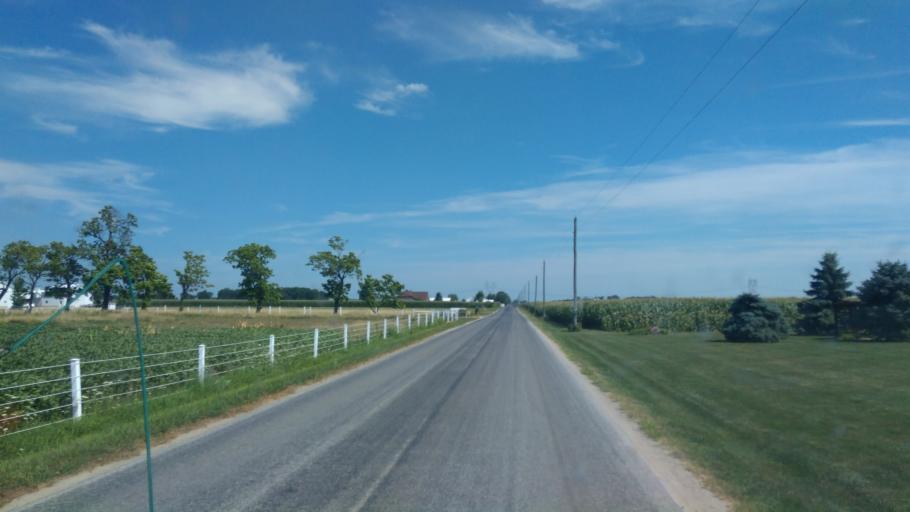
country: US
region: Indiana
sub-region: Adams County
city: Berne
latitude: 40.7016
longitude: -84.9750
